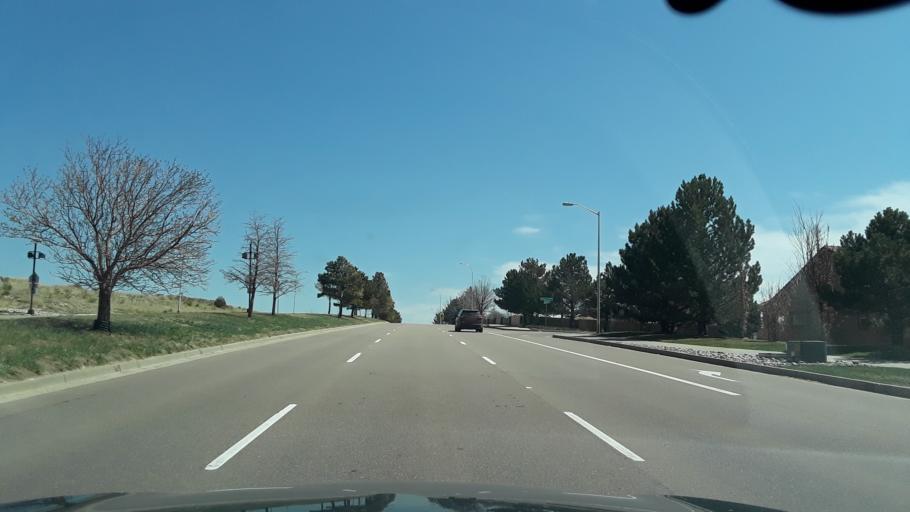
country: US
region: Colorado
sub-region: El Paso County
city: Black Forest
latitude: 38.9545
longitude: -104.7375
